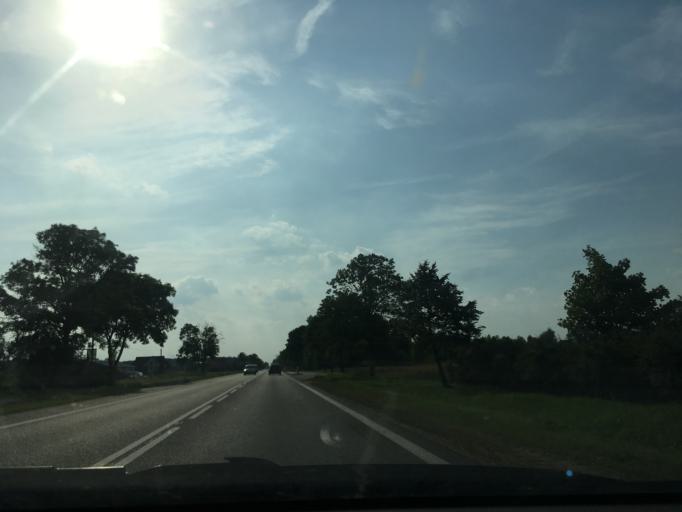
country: PL
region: Podlasie
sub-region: Powiat bialostocki
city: Suprasl
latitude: 53.1254
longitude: 23.2855
